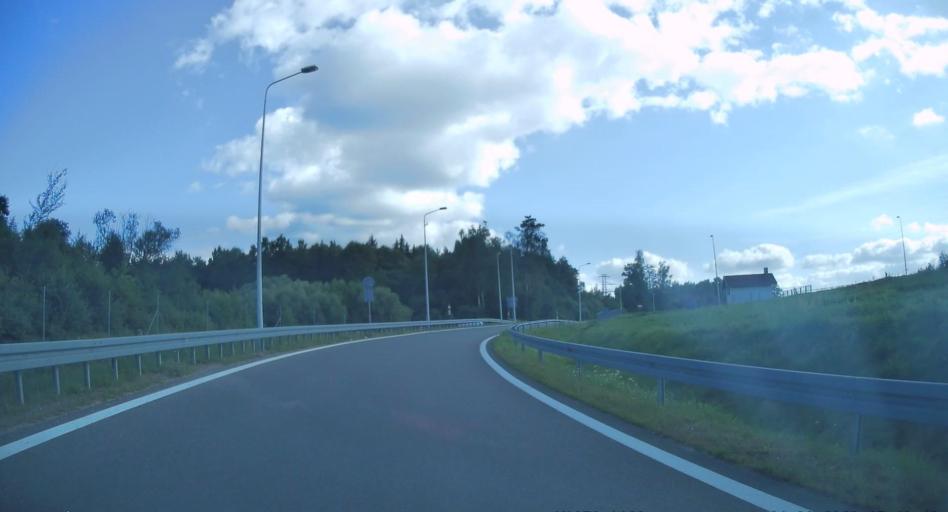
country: PL
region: Swietokrzyskie
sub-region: Powiat skarzyski
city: Suchedniow
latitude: 51.0490
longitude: 20.8231
